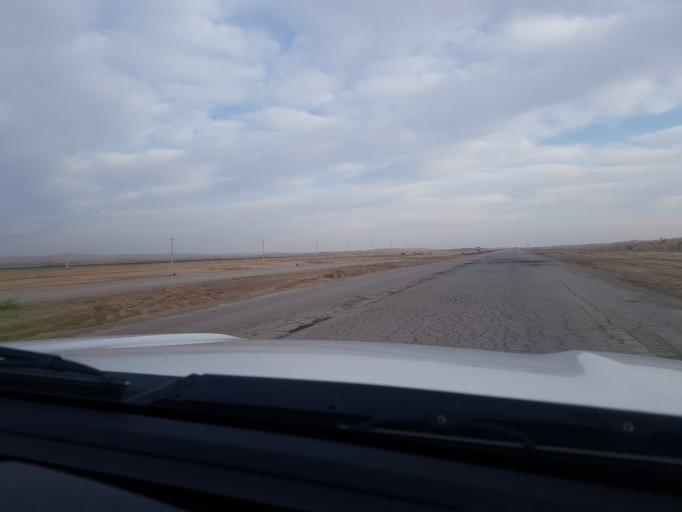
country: TM
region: Ahal
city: Abadan
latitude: 38.5889
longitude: 58.5023
